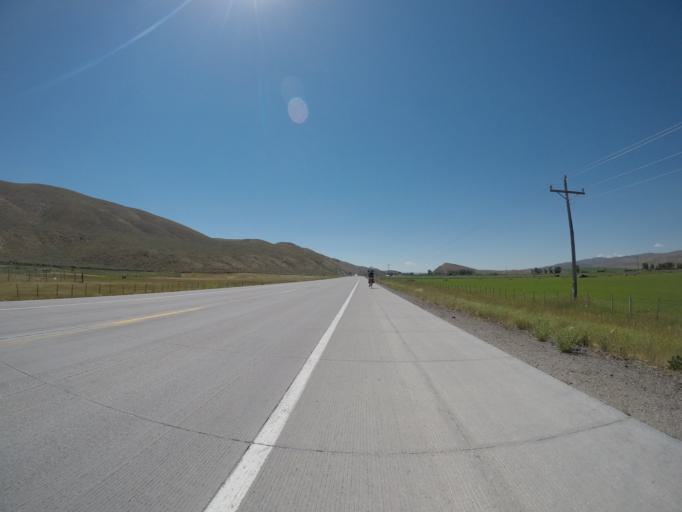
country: US
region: Idaho
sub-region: Bear Lake County
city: Montpelier
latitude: 42.1493
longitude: -110.9787
